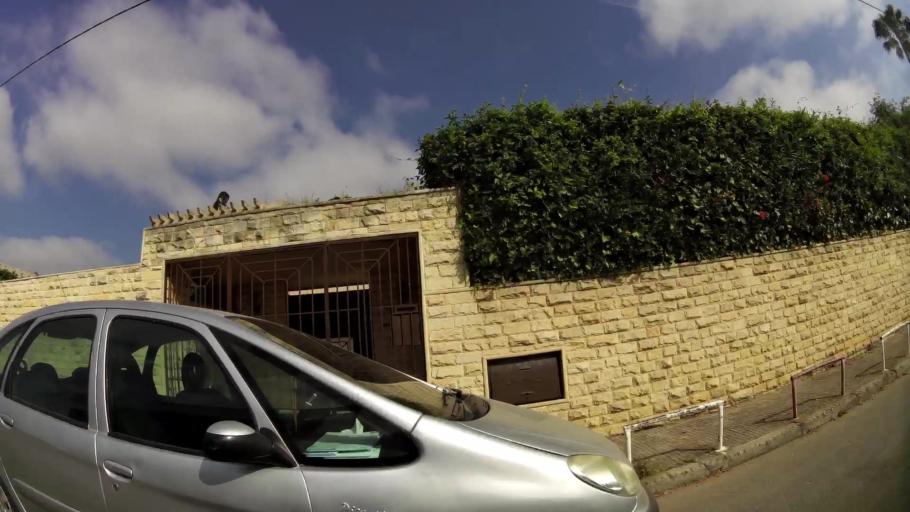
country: MA
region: Rabat-Sale-Zemmour-Zaer
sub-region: Rabat
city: Rabat
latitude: 33.9704
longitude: -6.8612
